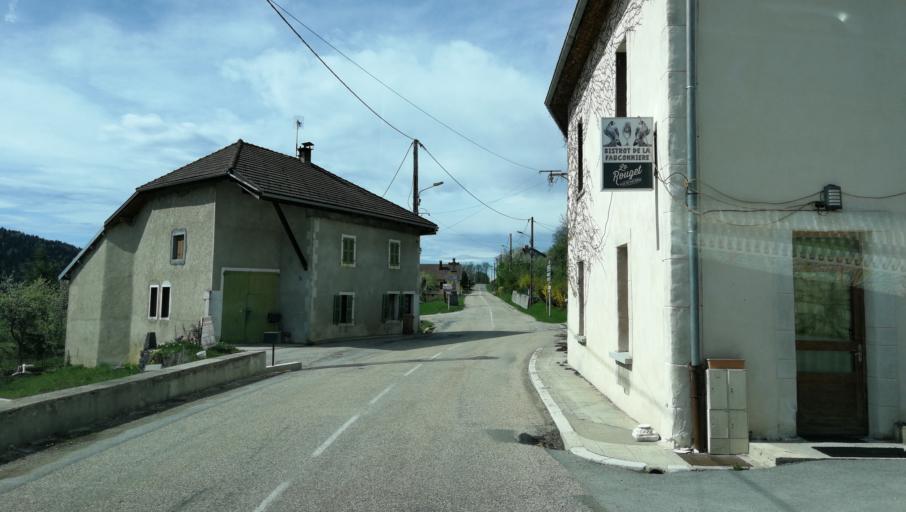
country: FR
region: Rhone-Alpes
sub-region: Departement de l'Ain
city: Arbent
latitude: 46.2503
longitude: 5.7754
